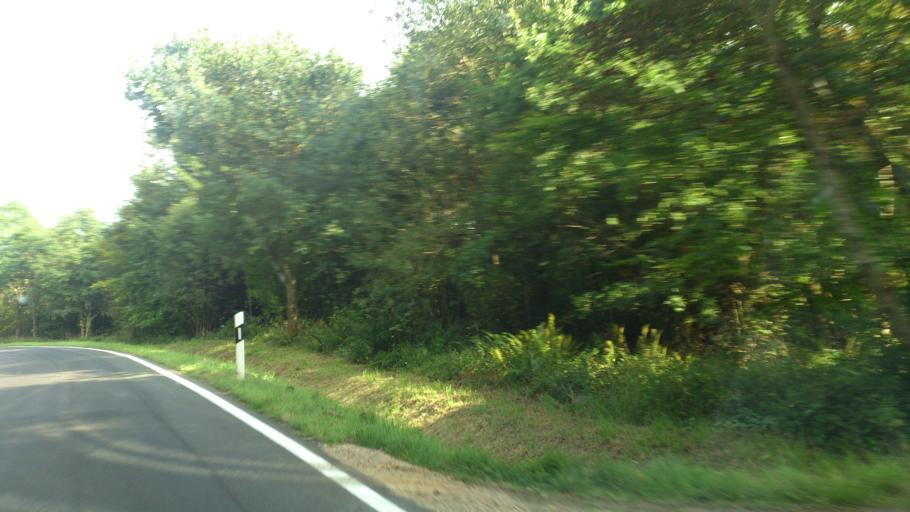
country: DE
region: Rheinland-Pfalz
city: Bongard
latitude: 50.3031
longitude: 6.8127
